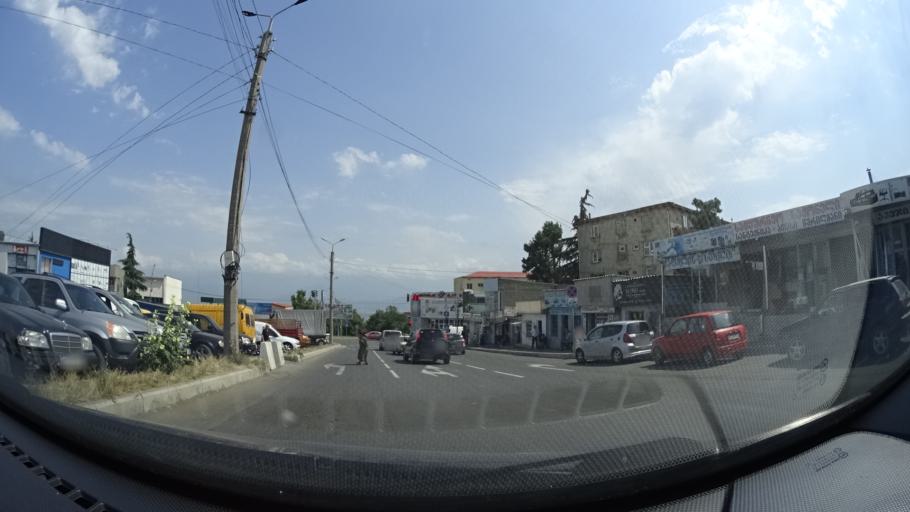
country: GE
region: Kakheti
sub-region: Telavi
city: Telavi
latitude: 41.9243
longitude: 45.4718
